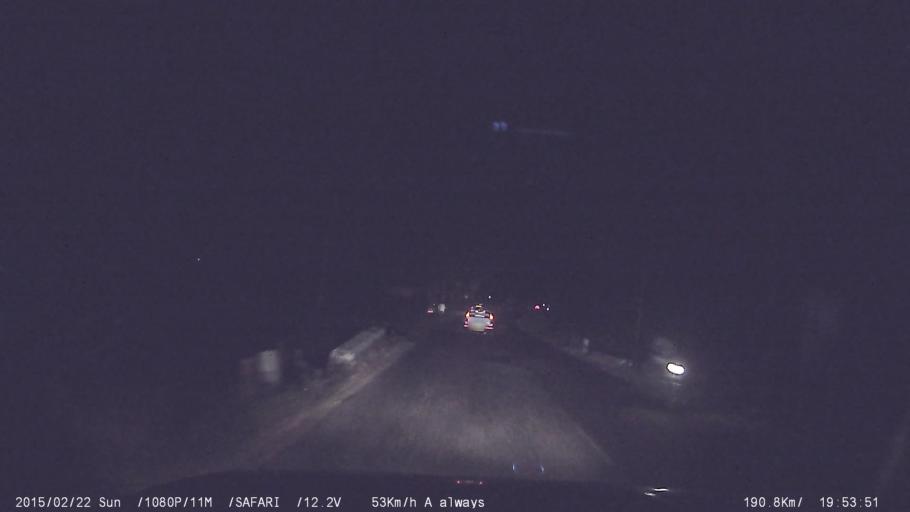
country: IN
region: Tamil Nadu
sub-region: Dindigul
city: Vattalkundu
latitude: 10.1637
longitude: 77.7381
